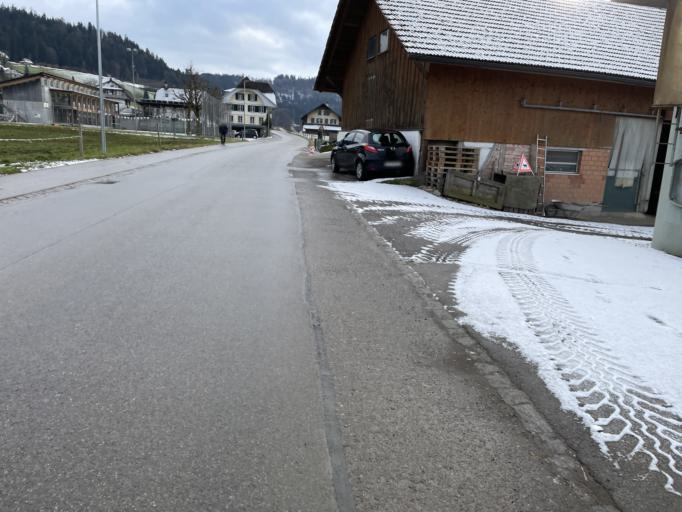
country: CH
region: Lucerne
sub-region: Entlebuch District
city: Oberdiessbach
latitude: 46.8188
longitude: 7.6138
